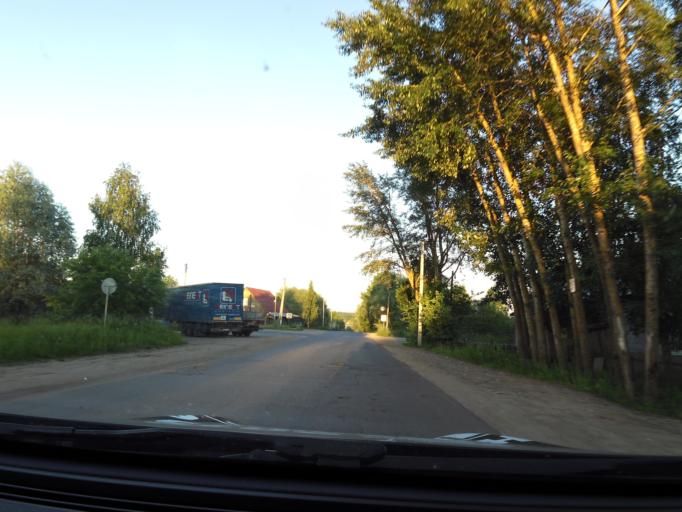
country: RU
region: Jaroslavl
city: Prechistoye
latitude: 58.4203
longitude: 40.3400
